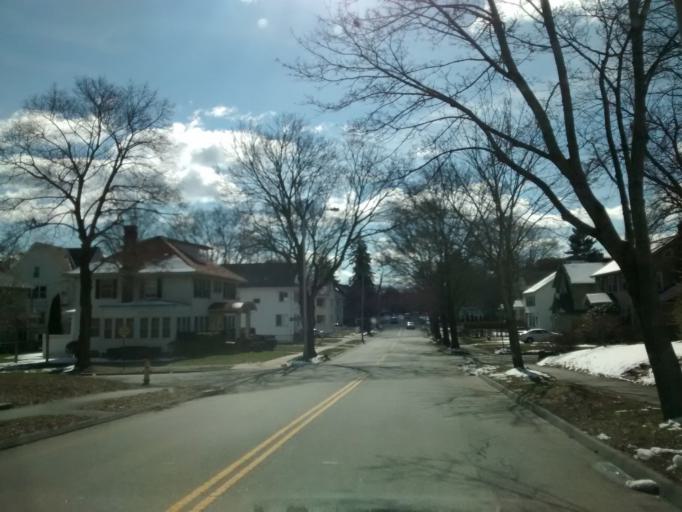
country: US
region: Massachusetts
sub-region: Worcester County
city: Worcester
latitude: 42.2642
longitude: -71.8380
